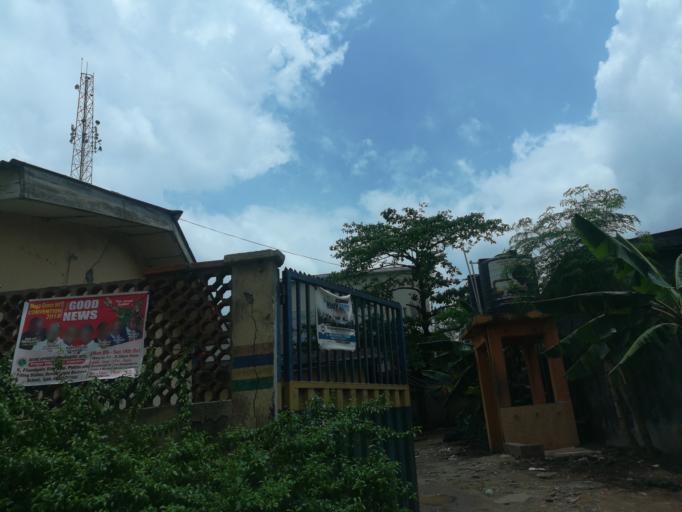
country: NG
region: Lagos
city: Somolu
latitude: 6.5527
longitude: 3.3596
